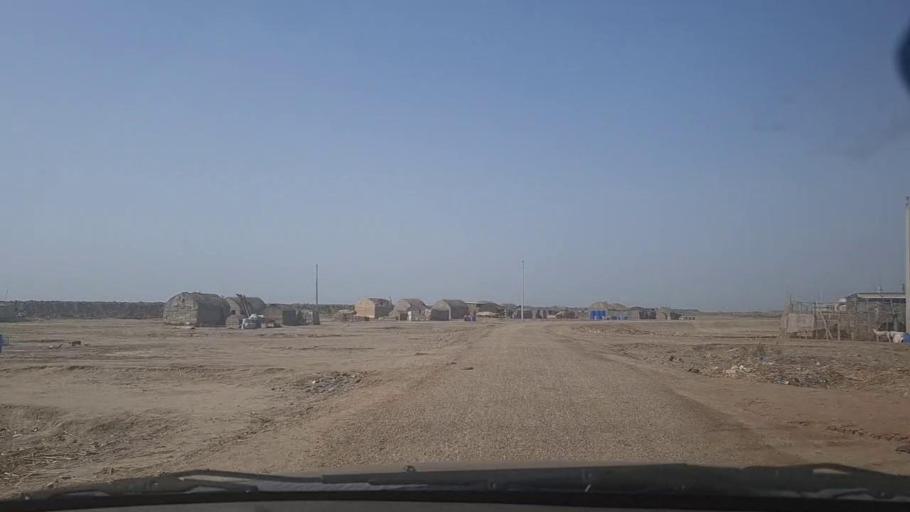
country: PK
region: Sindh
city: Keti Bandar
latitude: 24.1813
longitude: 67.5024
